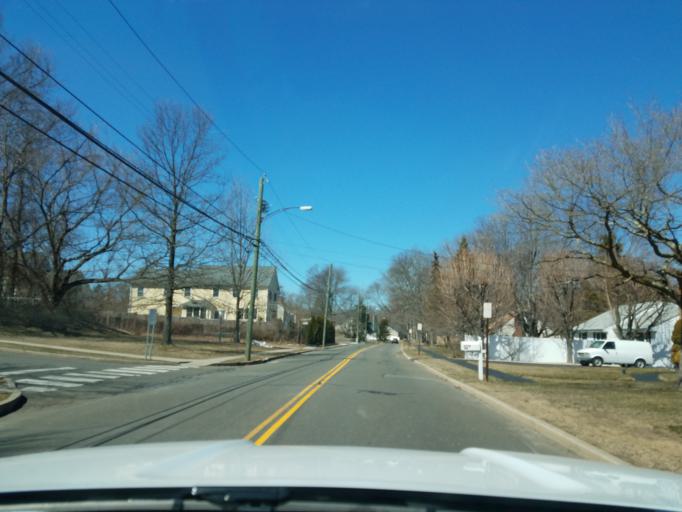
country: US
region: Connecticut
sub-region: Fairfield County
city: Fairfield
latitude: 41.1777
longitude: -73.2557
